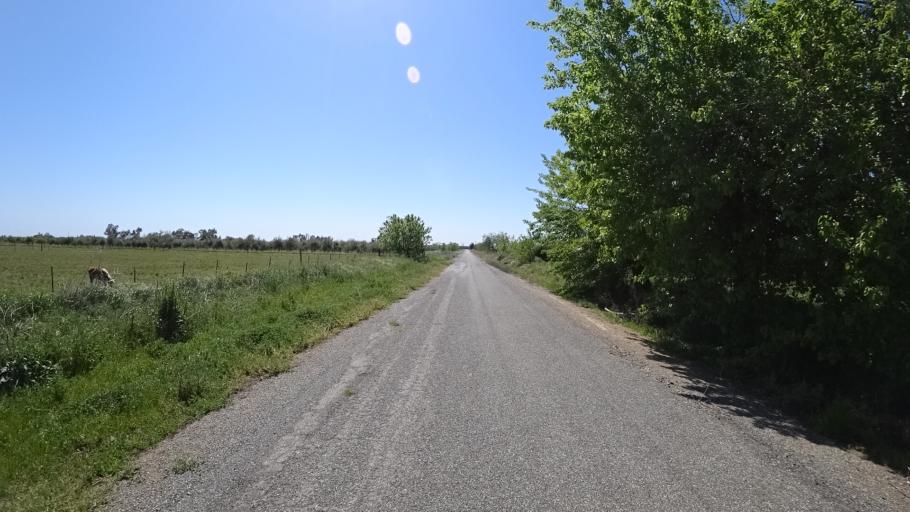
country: US
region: California
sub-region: Glenn County
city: Orland
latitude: 39.7769
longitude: -122.1830
